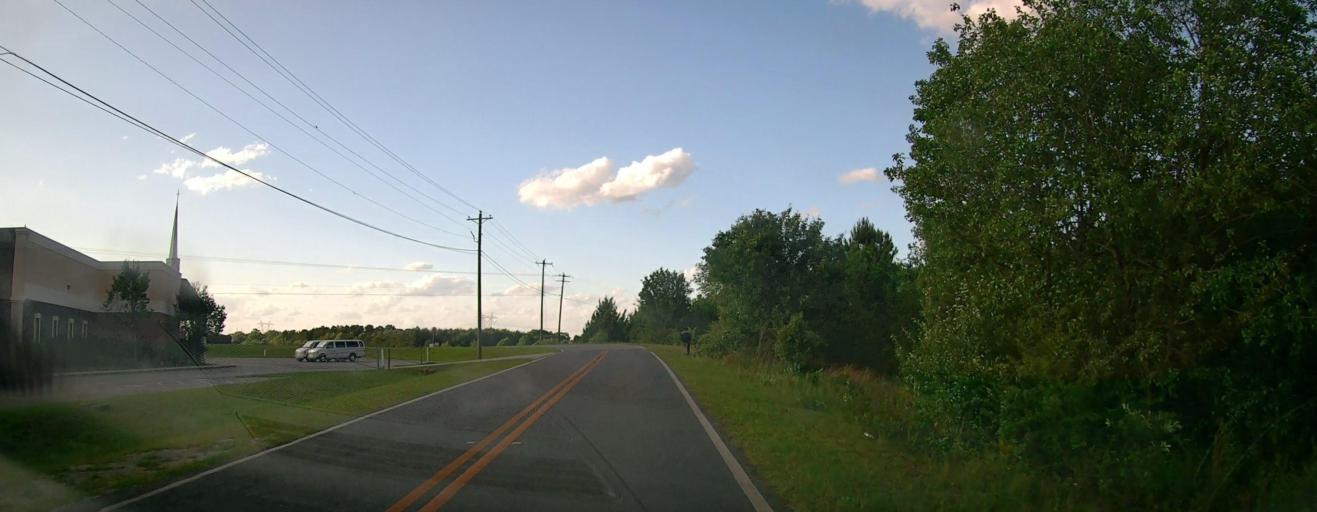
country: US
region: Georgia
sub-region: Peach County
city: Byron
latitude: 32.6368
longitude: -83.7671
